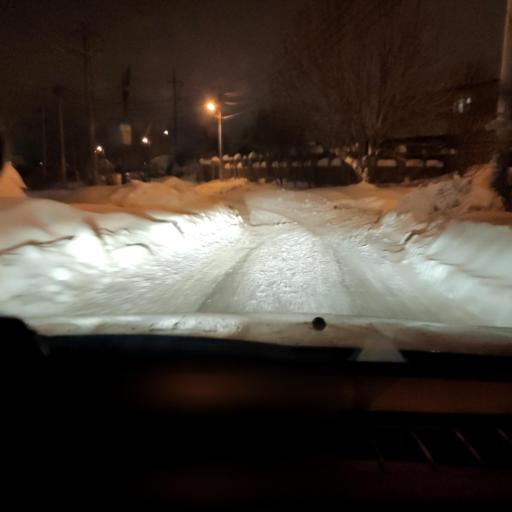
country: RU
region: Samara
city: Petra-Dubrava
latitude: 53.2911
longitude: 50.3118
